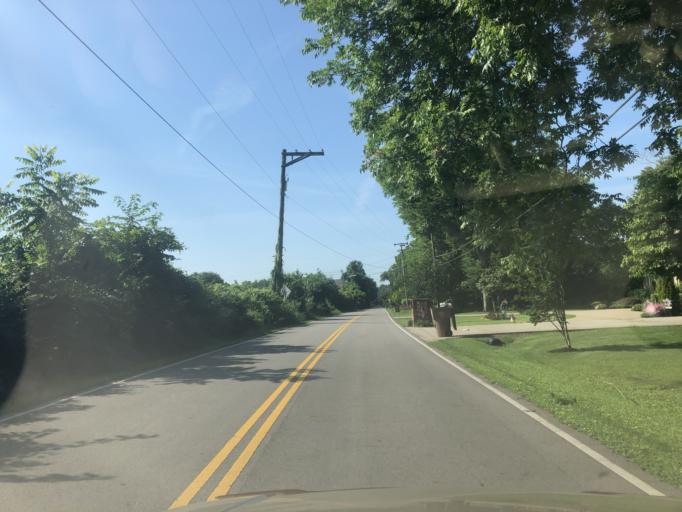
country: US
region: Tennessee
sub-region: Davidson County
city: Lakewood
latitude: 36.2258
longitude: -86.7071
